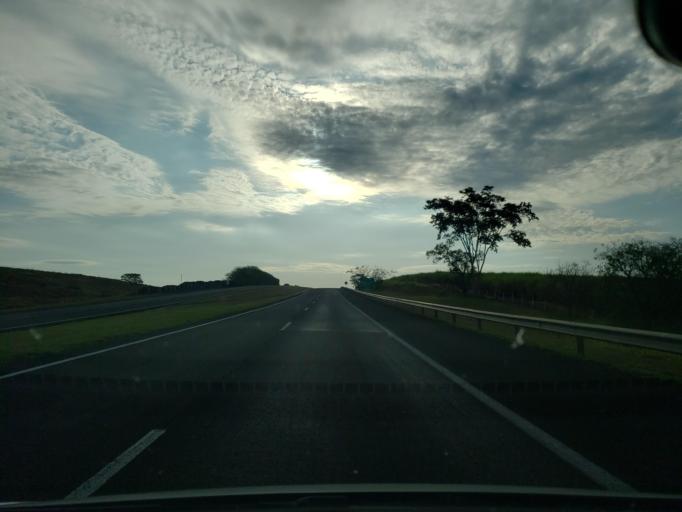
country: BR
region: Sao Paulo
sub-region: Mirandopolis
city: Mirandopolis
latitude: -21.0916
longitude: -51.0542
